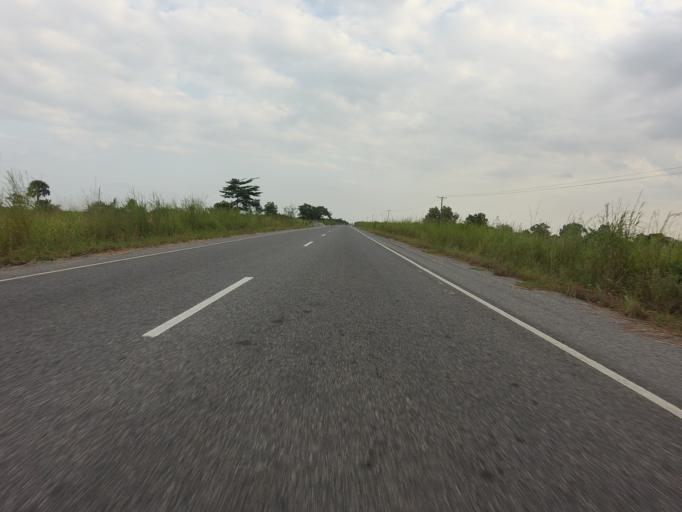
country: GH
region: Volta
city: Ho
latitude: 6.2436
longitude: 0.5509
